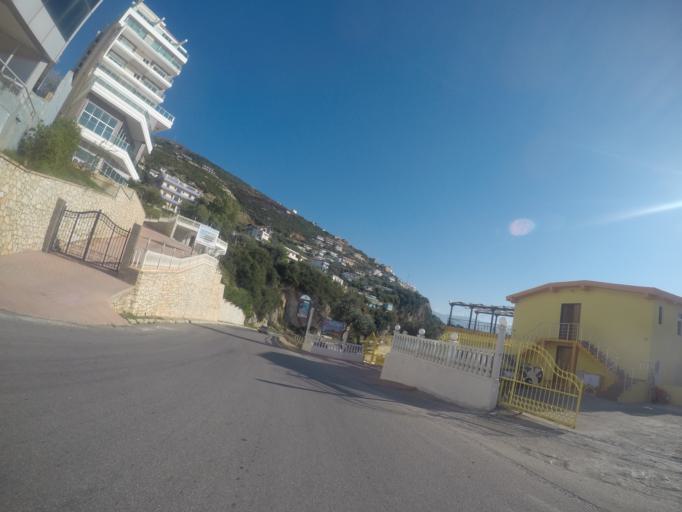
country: AL
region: Vlore
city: Vlore
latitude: 40.4133
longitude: 19.4806
